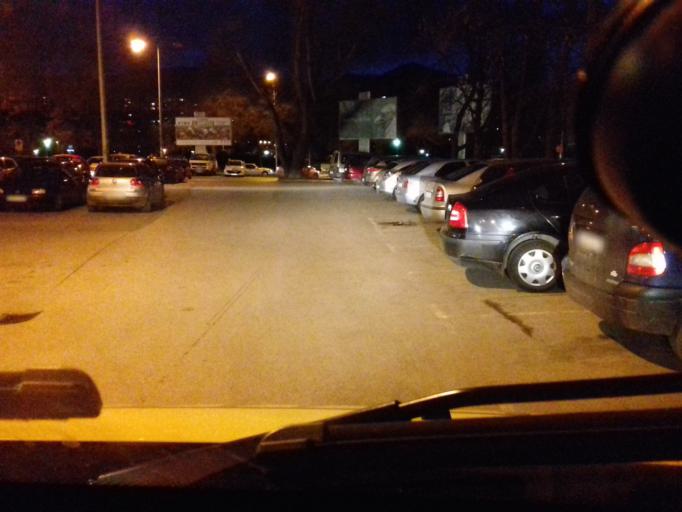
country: BA
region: Federation of Bosnia and Herzegovina
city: Zenica
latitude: 44.2037
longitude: 17.9115
